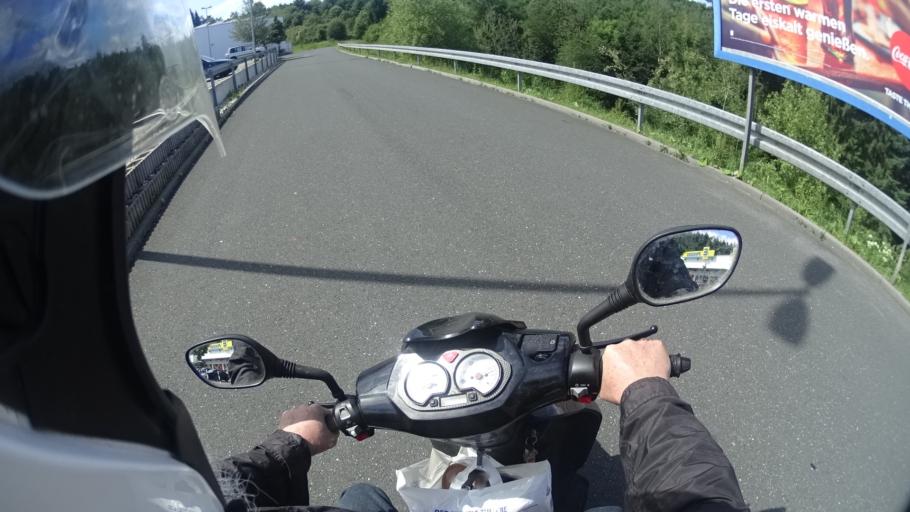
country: DE
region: Hesse
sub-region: Regierungsbezirk Darmstadt
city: Bad Schwalbach
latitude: 50.1437
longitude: 8.0444
